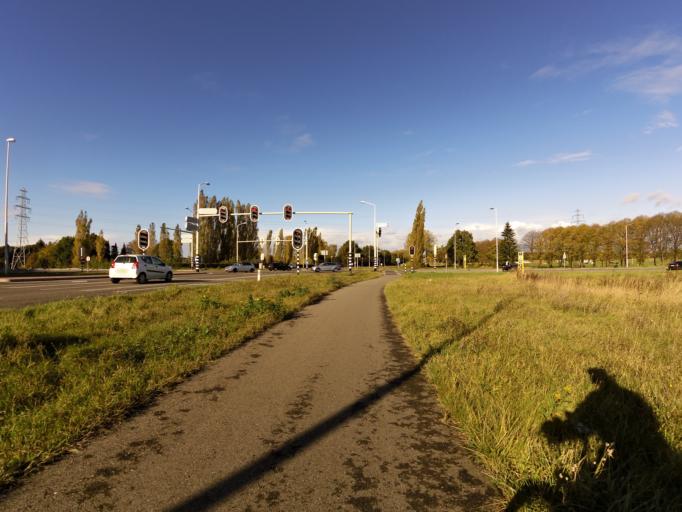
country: NL
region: Gelderland
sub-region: Gemeente Doetinchem
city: Doetinchem
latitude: 51.9459
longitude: 6.2196
